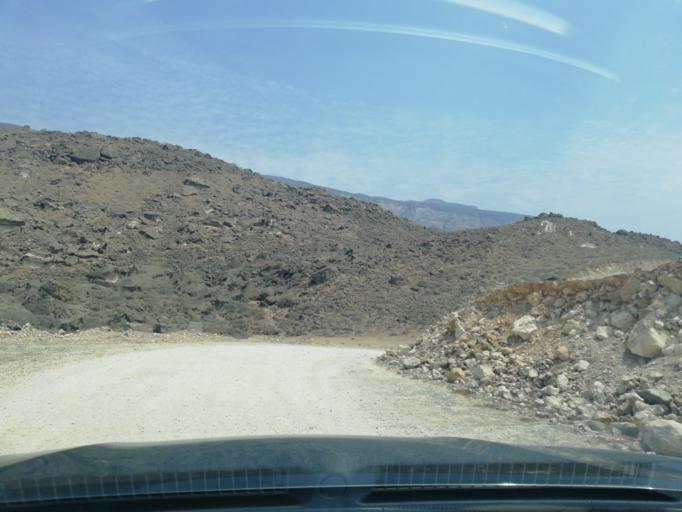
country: OM
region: Zufar
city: Salalah
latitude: 16.8180
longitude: 53.6940
